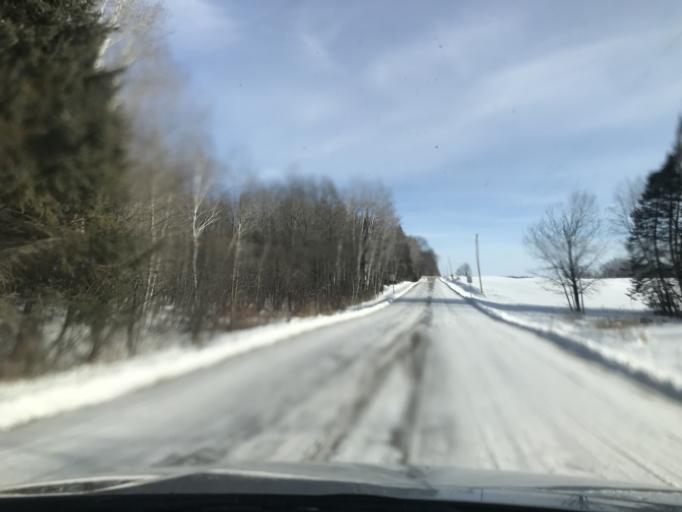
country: US
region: Wisconsin
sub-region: Oconto County
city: Gillett
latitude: 45.1201
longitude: -88.2459
